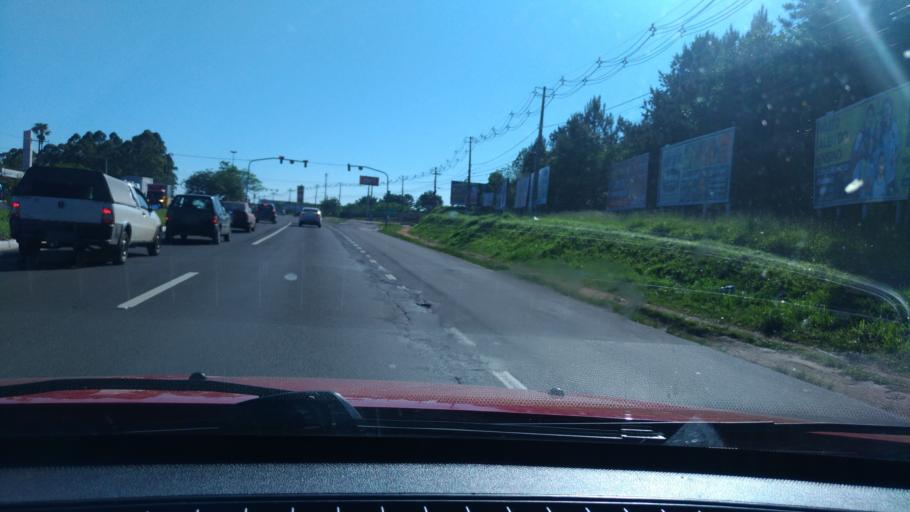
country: BR
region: Rio Grande do Sul
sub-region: Viamao
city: Viamao
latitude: -30.0871
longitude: -51.0581
